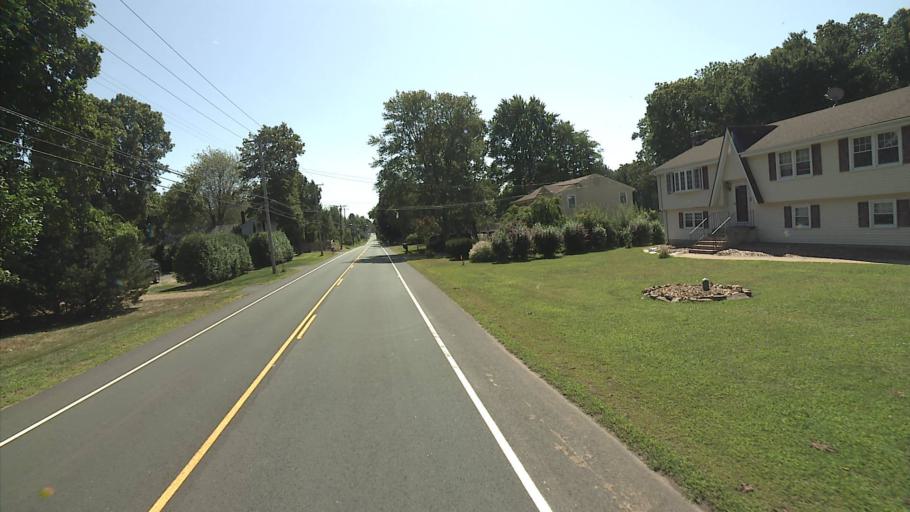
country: US
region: Connecticut
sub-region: Hartford County
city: Windsor Locks
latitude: 41.8979
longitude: -72.6261
